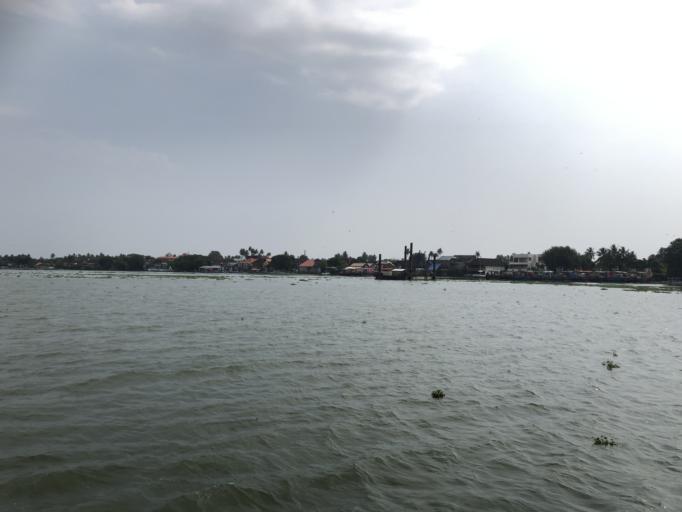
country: IN
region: Kerala
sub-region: Ernakulam
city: Cochin
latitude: 9.9695
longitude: 76.2544
